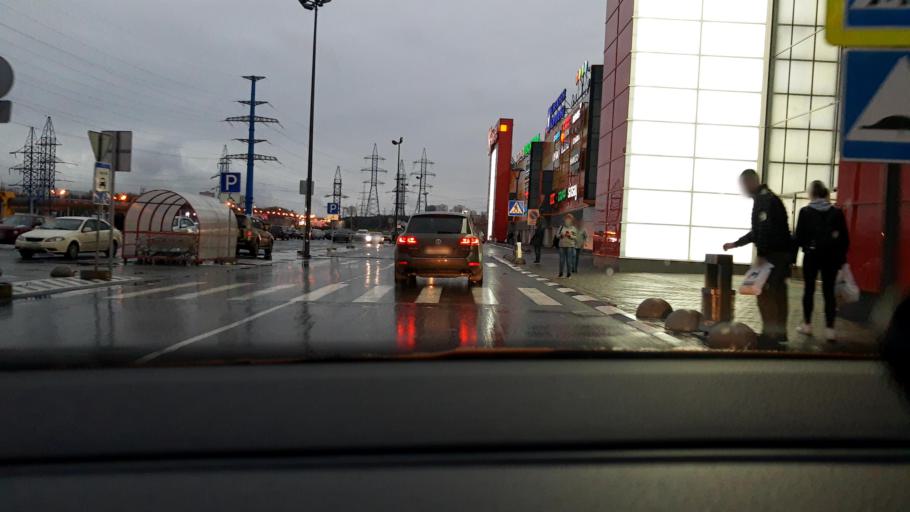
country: RU
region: Moscow
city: Lianozovo
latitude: 55.9124
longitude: 37.5852
